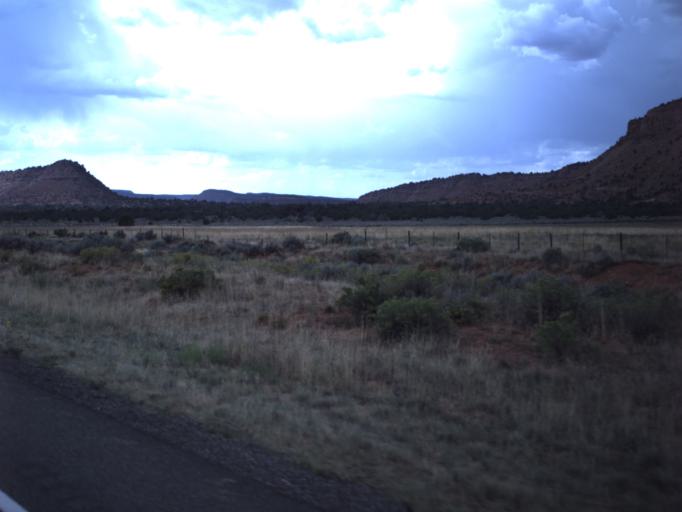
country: US
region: Utah
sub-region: Kane County
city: Kanab
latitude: 37.0386
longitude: -112.3192
